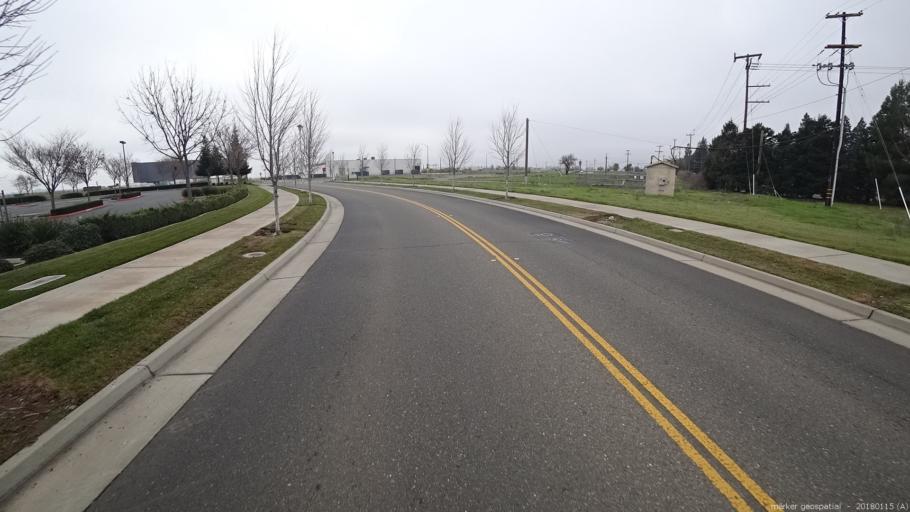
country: US
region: California
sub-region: Sacramento County
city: Rancho Cordova
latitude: 38.5674
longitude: -121.3054
